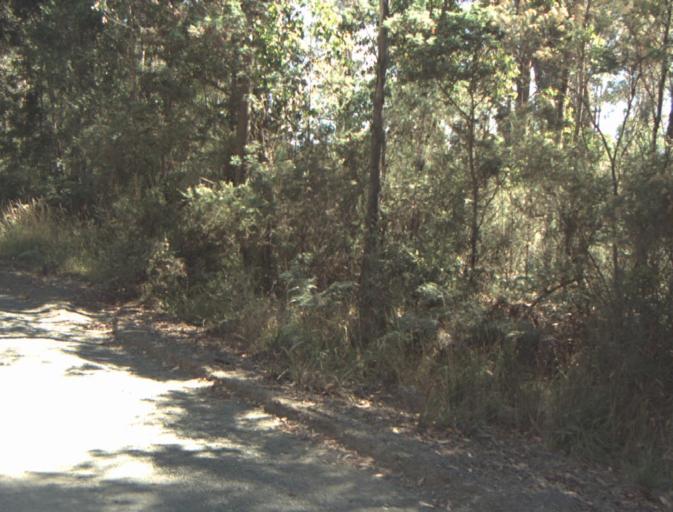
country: AU
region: Tasmania
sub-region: Launceston
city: Newstead
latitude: -41.3640
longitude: 147.2312
